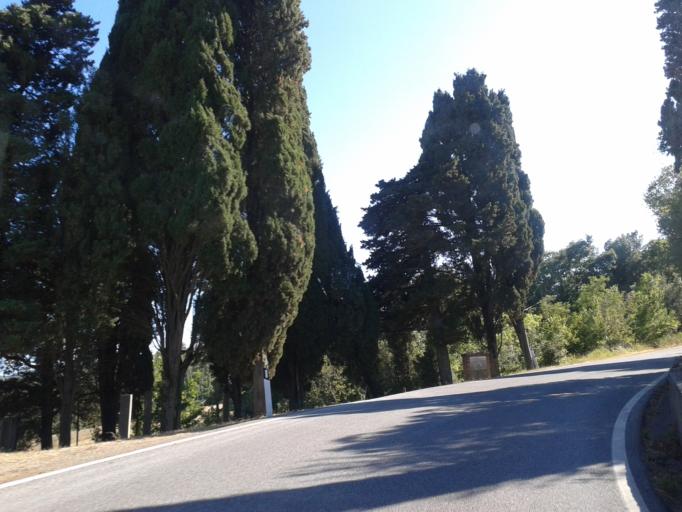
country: IT
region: Tuscany
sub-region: Province of Pisa
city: Chianni
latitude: 43.4406
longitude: 10.6235
